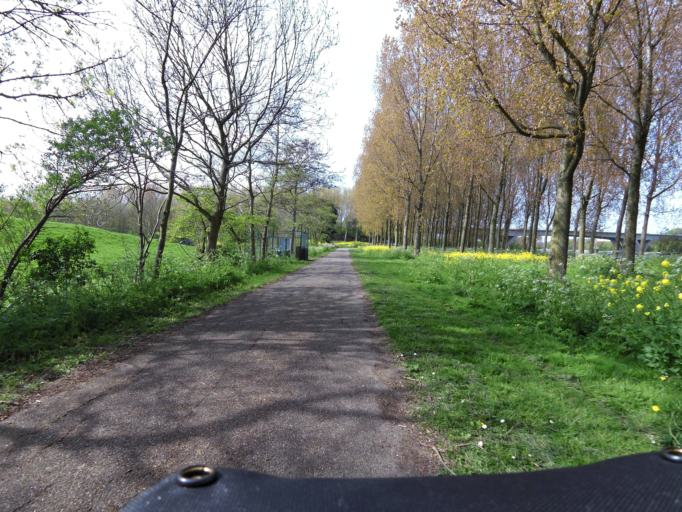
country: NL
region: South Holland
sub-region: Gemeente Brielle
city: Brielle
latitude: 51.8967
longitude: 4.2077
